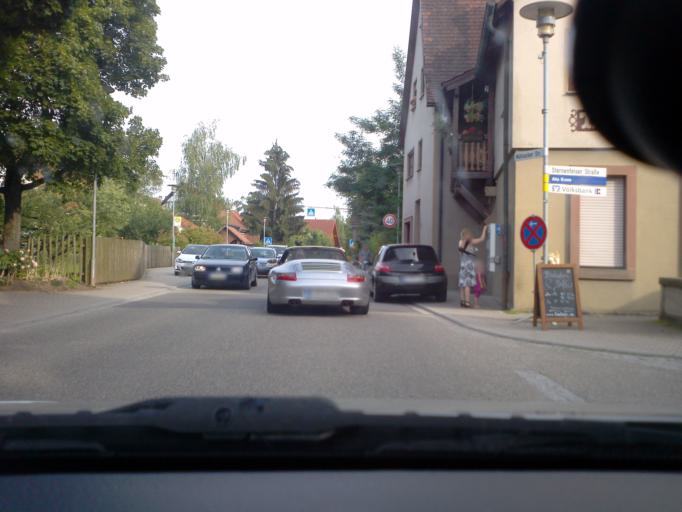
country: DE
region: Baden-Wuerttemberg
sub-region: Karlsruhe Region
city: Sternenfels
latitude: 49.0269
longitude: 8.8531
